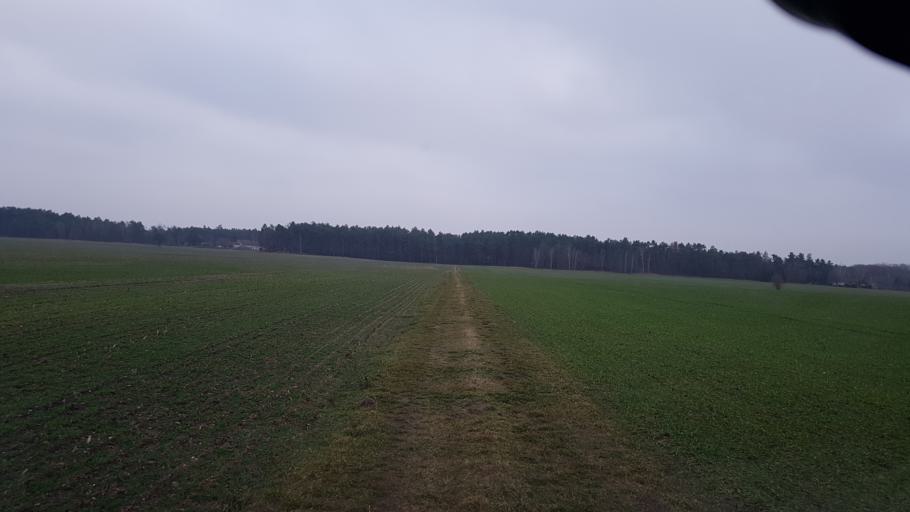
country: DE
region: Brandenburg
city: Schonewalde
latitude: 51.6426
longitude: 13.6177
